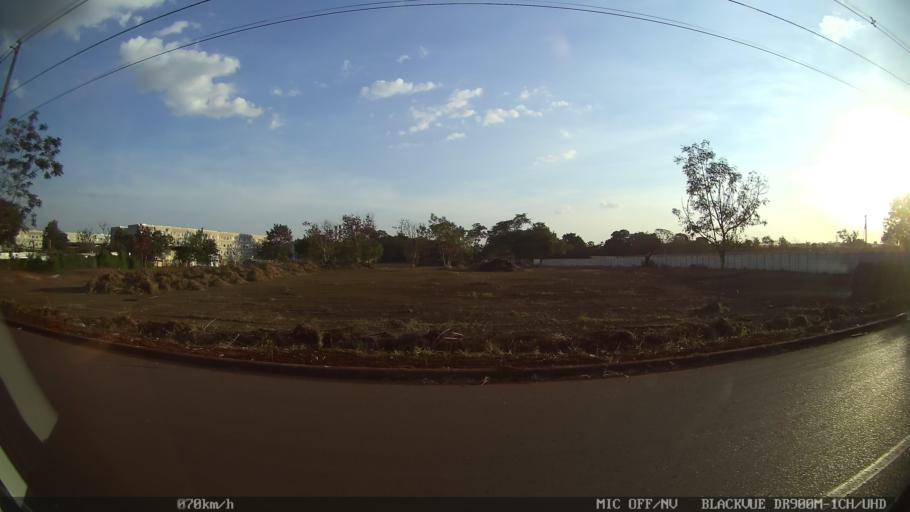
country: BR
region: Sao Paulo
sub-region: Ribeirao Preto
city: Ribeirao Preto
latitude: -21.1152
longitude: -47.8064
